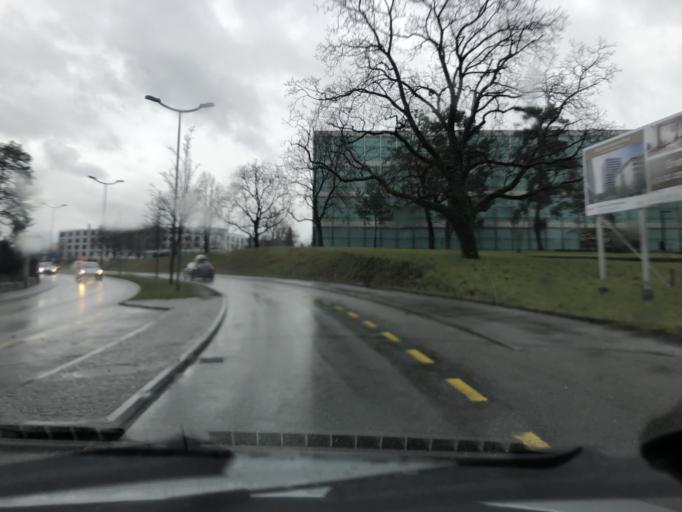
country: CH
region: Aargau
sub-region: Bezirk Brugg
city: Brugg
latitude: 47.4806
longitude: 8.2127
